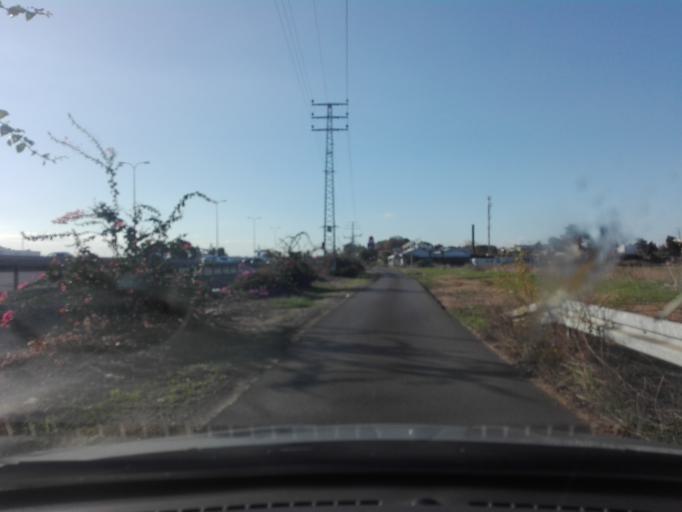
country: IL
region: Central District
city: Netanya
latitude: 32.3062
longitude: 34.8642
